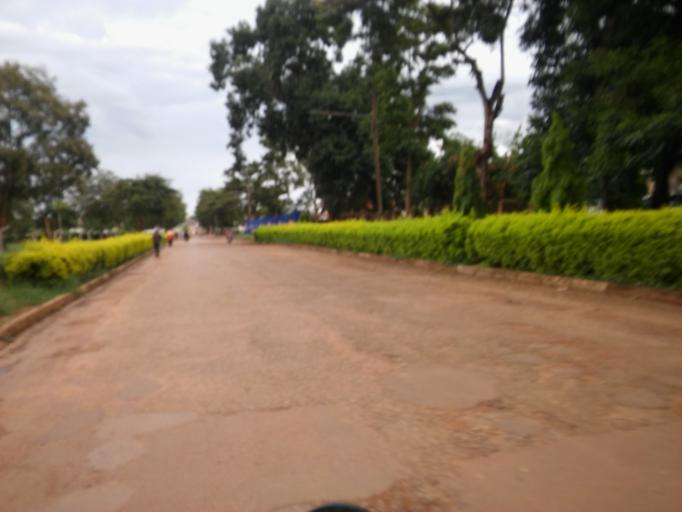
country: UG
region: Eastern Region
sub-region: Mbale District
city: Mbale
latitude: 1.0681
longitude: 34.1832
